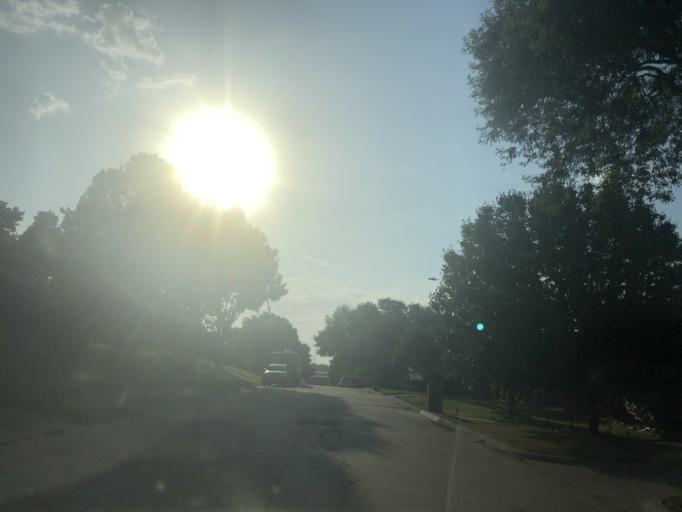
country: US
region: Texas
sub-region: Dallas County
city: Grand Prairie
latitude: 32.7702
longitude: -97.0309
